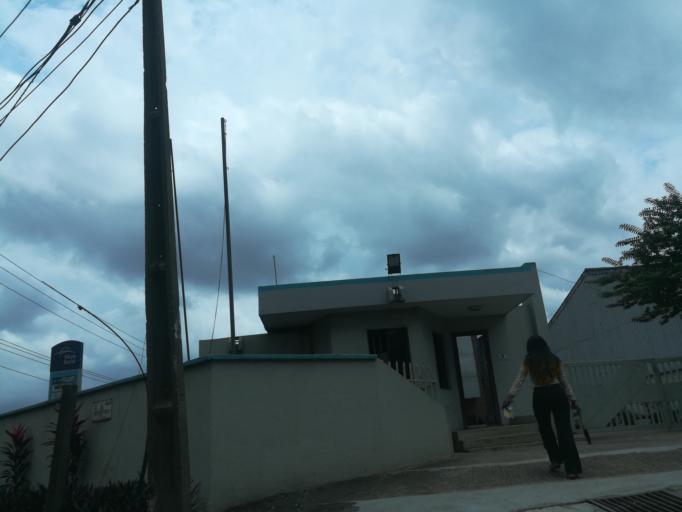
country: NG
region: Lagos
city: Oshodi
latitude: 6.5517
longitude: 3.3556
